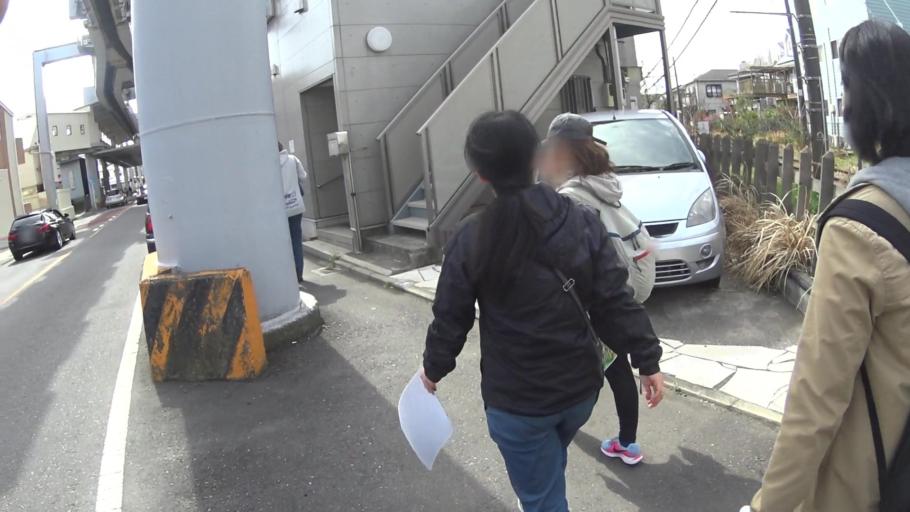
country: JP
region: Kanagawa
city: Kamakura
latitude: 35.3449
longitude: 139.5288
